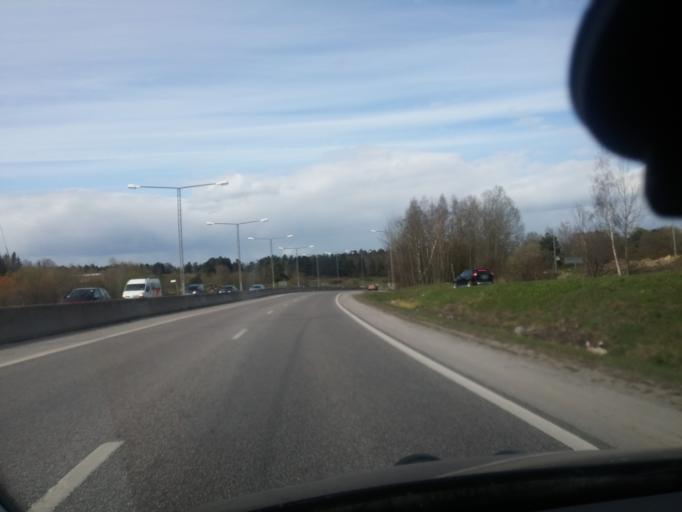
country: SE
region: Stockholm
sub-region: Stockholms Kommun
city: Kista
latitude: 59.3761
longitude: 17.9273
